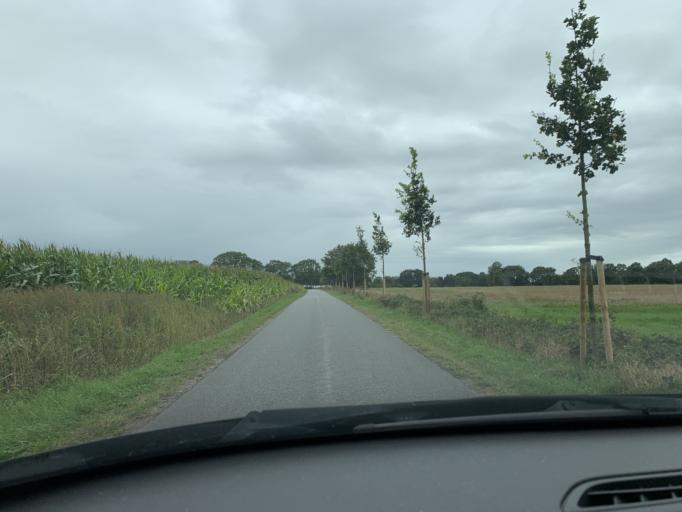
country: DE
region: Lower Saxony
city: Westerstede
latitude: 53.2617
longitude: 7.8823
